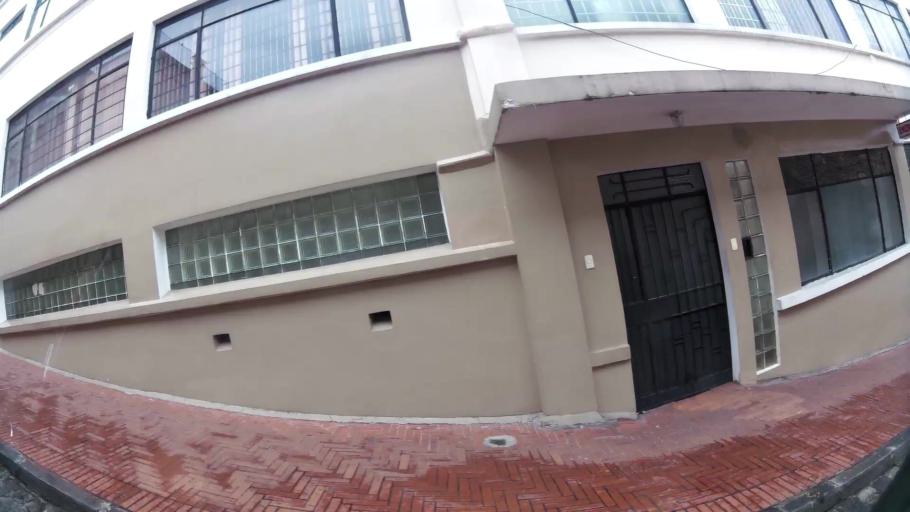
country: EC
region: Pichincha
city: Quito
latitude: -0.2167
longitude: -78.5101
